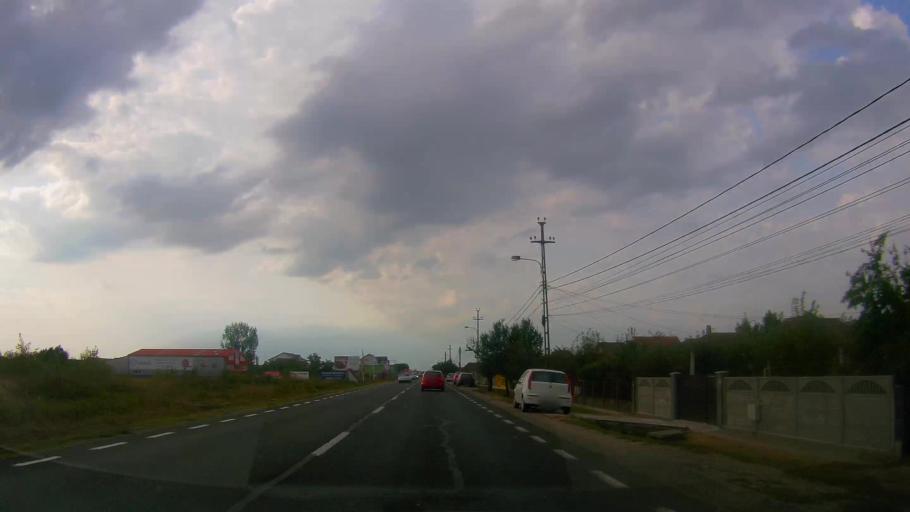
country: RO
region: Satu Mare
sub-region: Municipiul Satu Mare
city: Satu Mare
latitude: 47.7580
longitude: 22.8831
